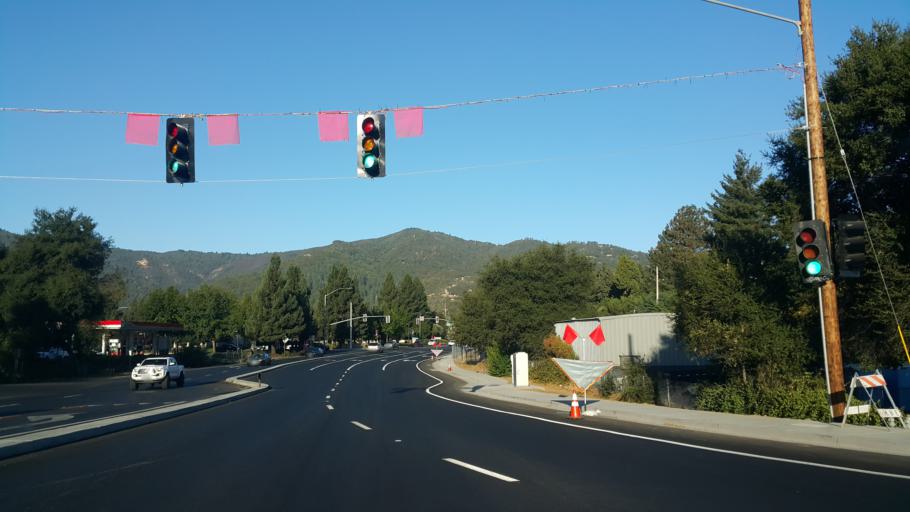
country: US
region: California
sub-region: Mendocino County
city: Ukiah
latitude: 39.1359
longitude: -123.1968
